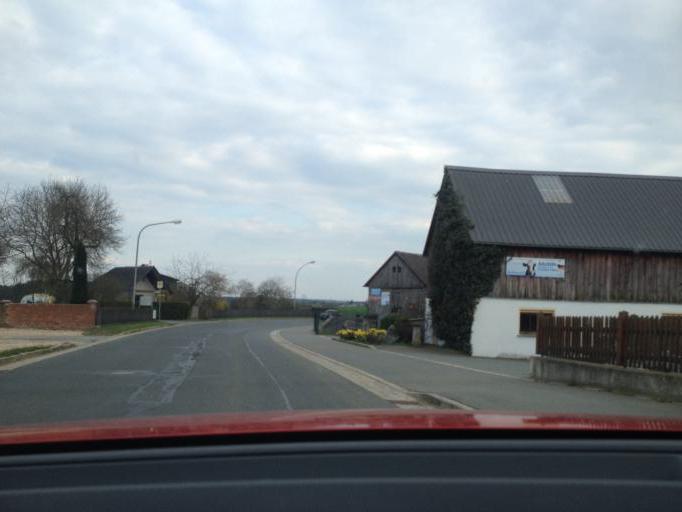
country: DE
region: Bavaria
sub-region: Upper Palatinate
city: Speinshart
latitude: 49.7675
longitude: 11.8182
